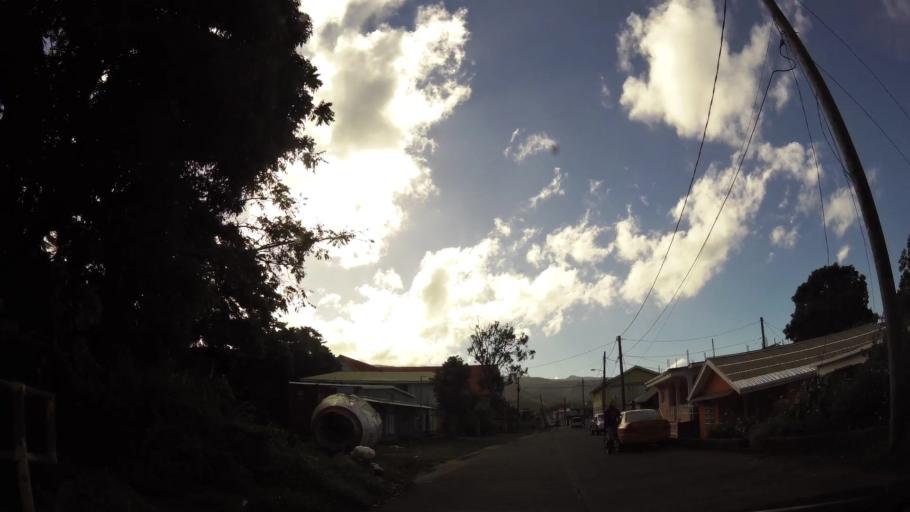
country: DM
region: Saint John
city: Portsmouth
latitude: 15.5783
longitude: -61.4566
